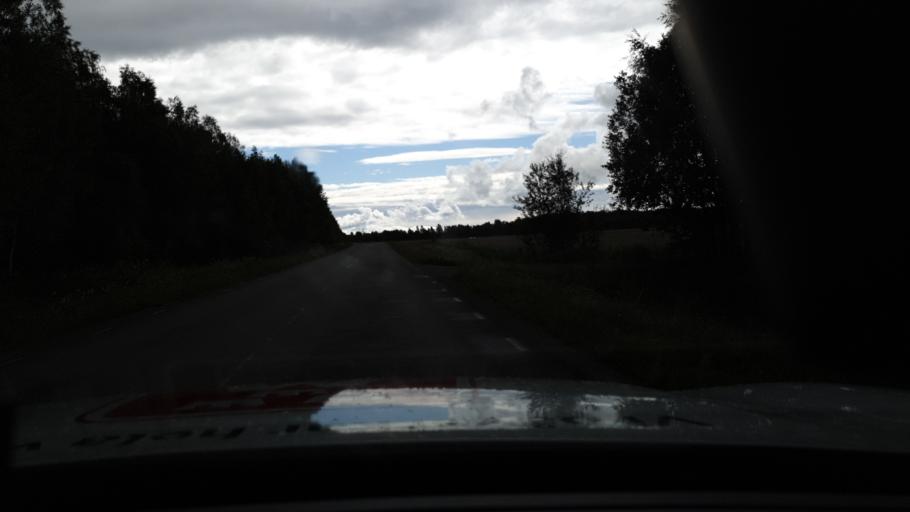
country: SE
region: Norrbotten
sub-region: Pitea Kommun
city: Rosvik
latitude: 65.5203
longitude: 21.8271
